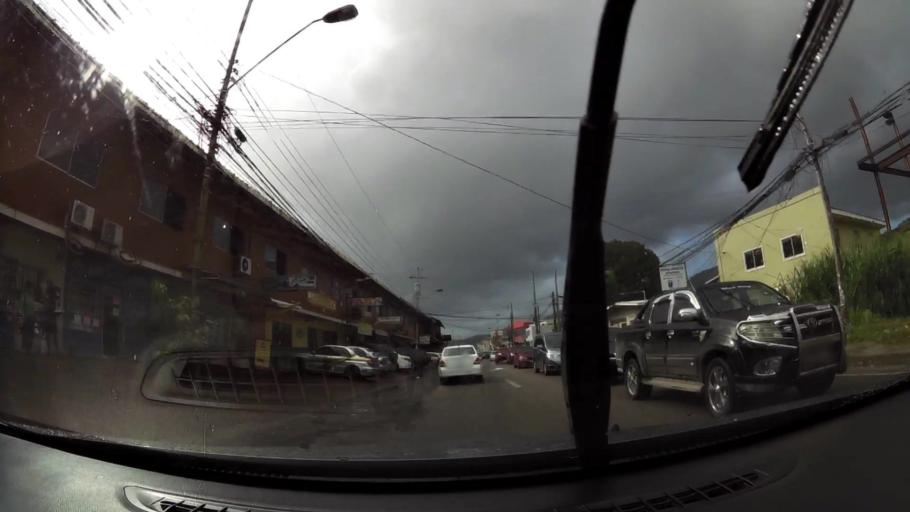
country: TT
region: Tunapuna/Piarco
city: Tunapuna
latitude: 10.6474
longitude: -61.4031
